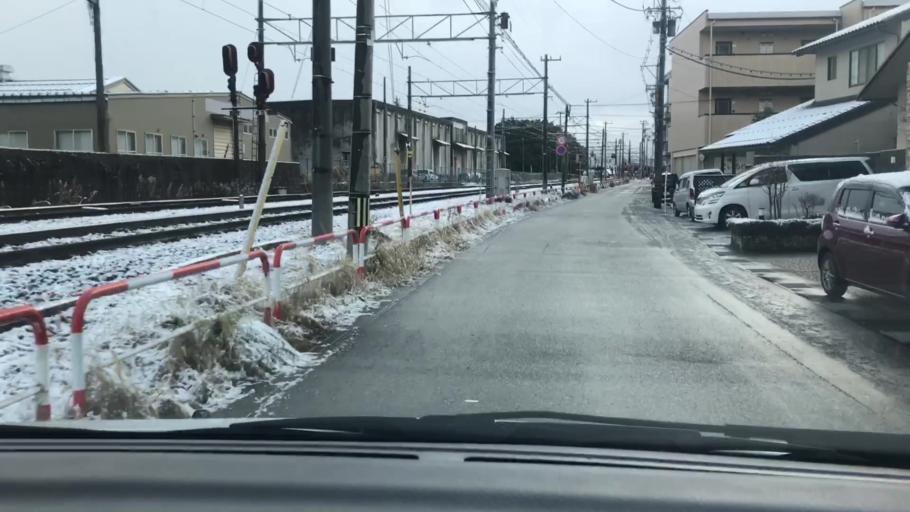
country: JP
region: Toyama
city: Toyama-shi
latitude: 36.6982
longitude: 137.2277
